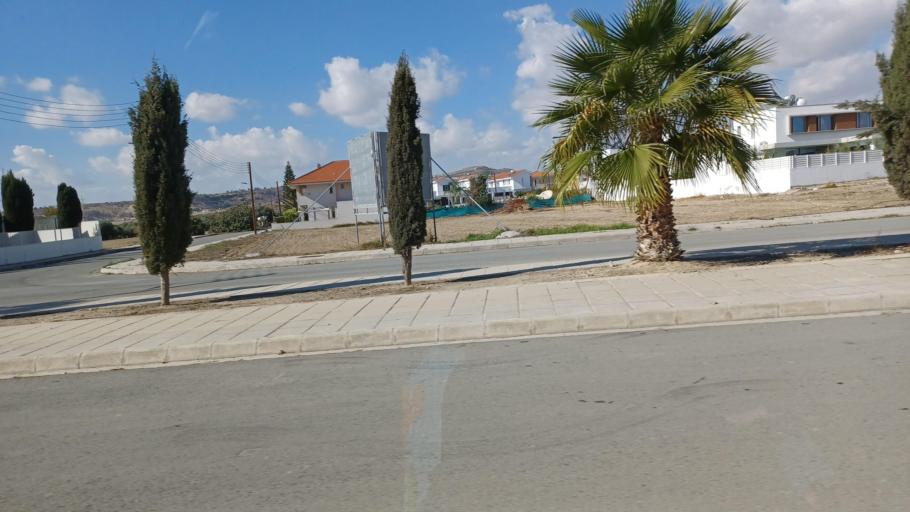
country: CY
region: Larnaka
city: Voroklini
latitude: 34.9857
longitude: 33.6793
